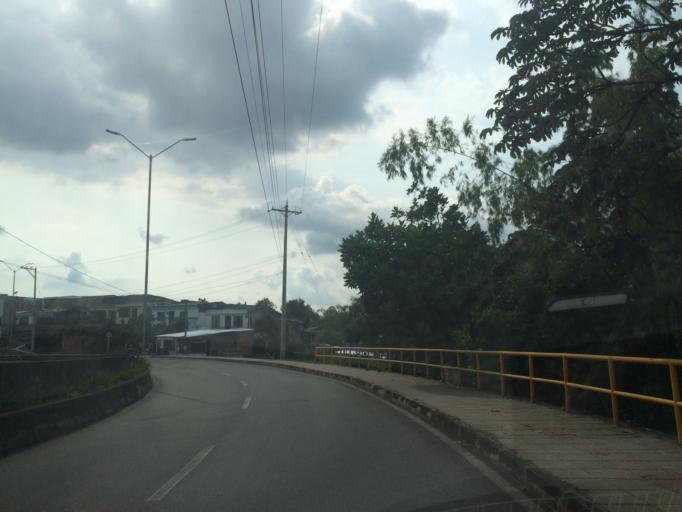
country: CO
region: Quindio
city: Armenia
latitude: 4.5186
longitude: -75.7026
